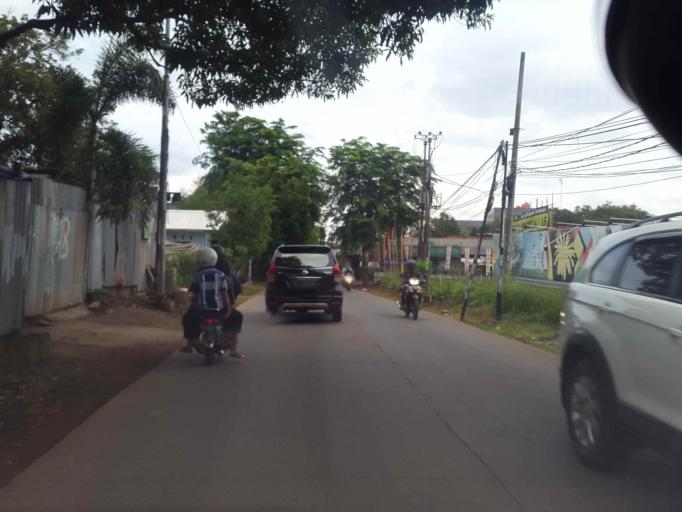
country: ID
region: West Java
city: Cileungsir
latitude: -6.3437
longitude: 106.9227
